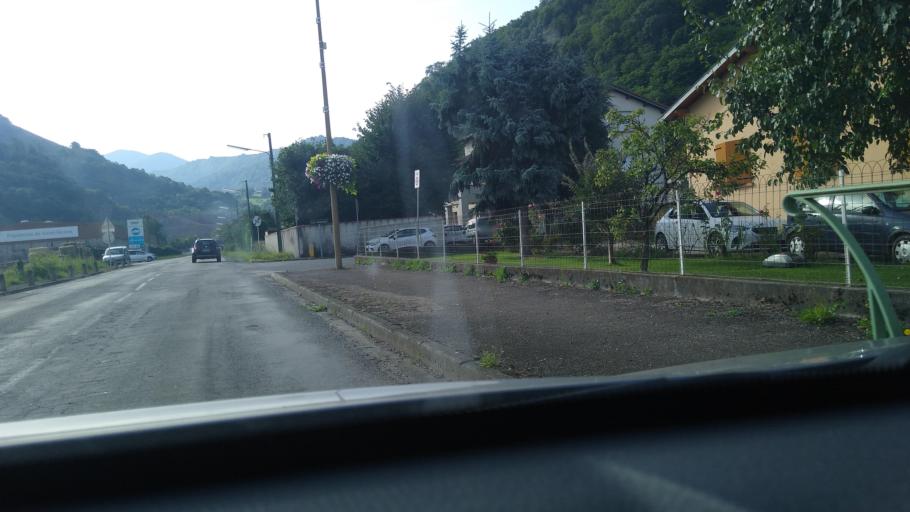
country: FR
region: Midi-Pyrenees
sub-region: Departement de l'Ariege
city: Saint-Girons
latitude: 42.9680
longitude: 1.1648
